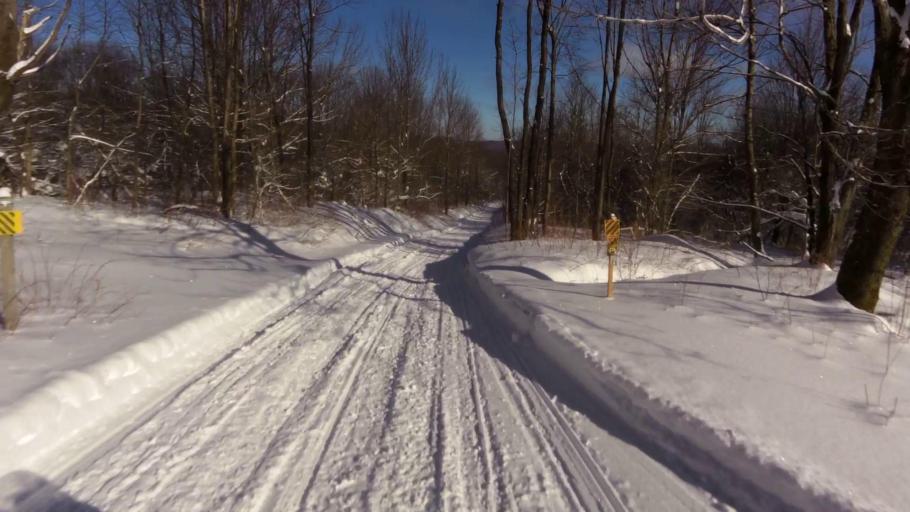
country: US
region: New York
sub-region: Chautauqua County
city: Falconer
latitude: 42.2792
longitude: -79.1284
